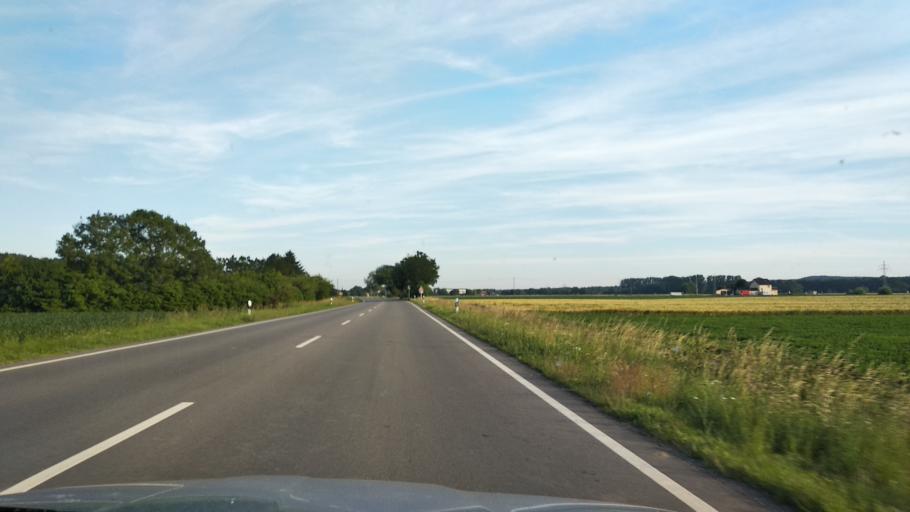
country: DE
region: Bavaria
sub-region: Swabia
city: Illertissen
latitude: 48.1926
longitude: 10.1053
